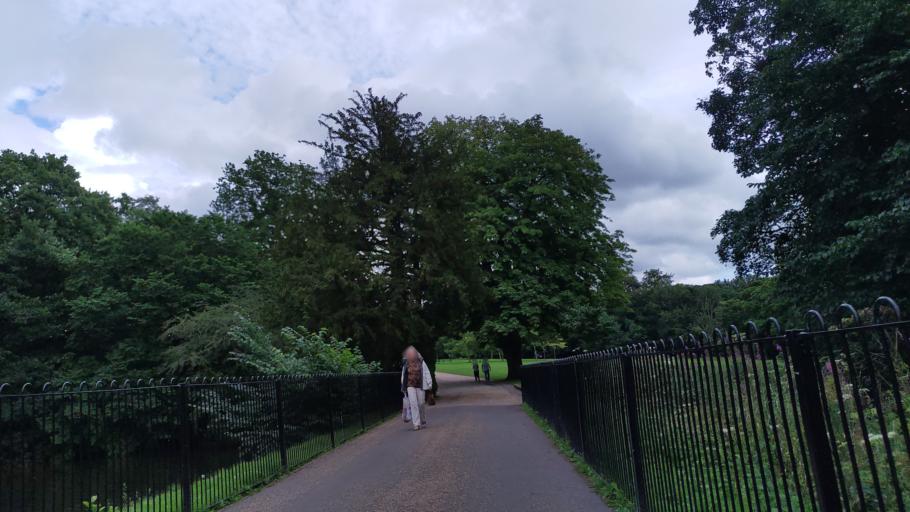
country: GB
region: England
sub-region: Lancashire
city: Chorley
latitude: 53.6585
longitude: -2.6451
